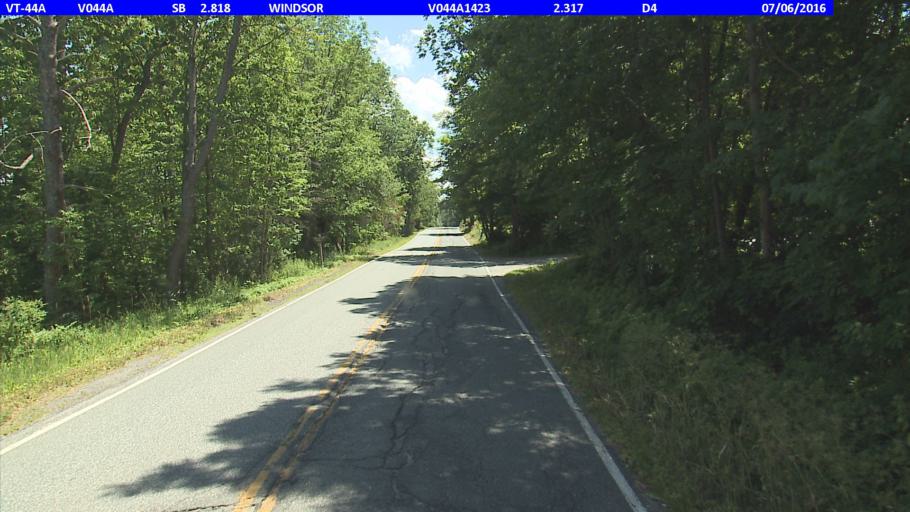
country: US
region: Vermont
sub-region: Windsor County
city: Windsor
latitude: 43.4573
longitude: -72.4221
